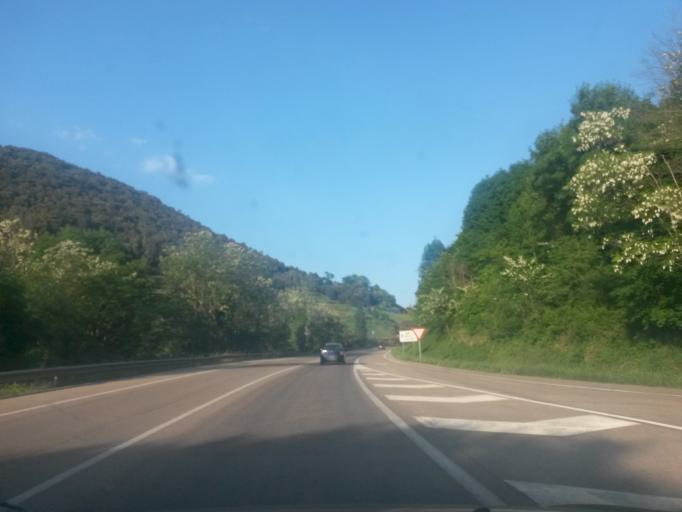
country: ES
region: Catalonia
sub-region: Provincia de Girona
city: Sant Joan les Fonts
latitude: 42.1920
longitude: 2.5140
